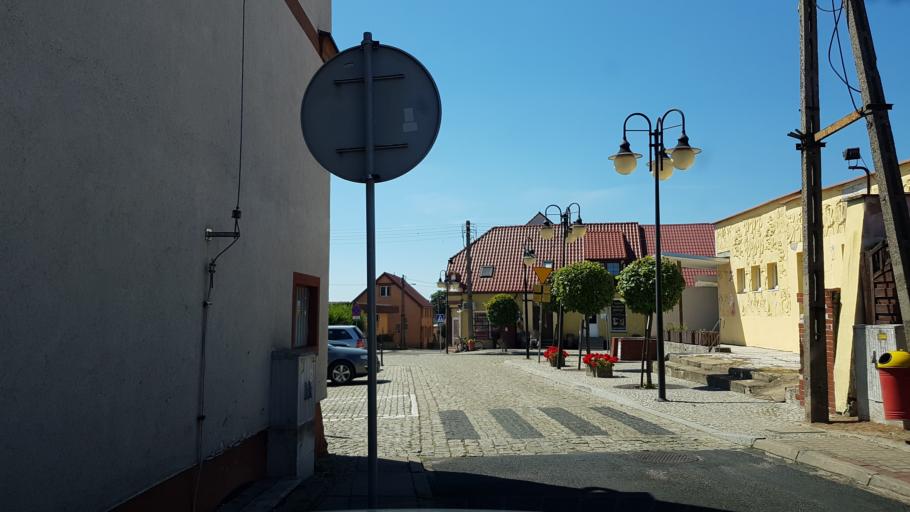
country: PL
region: West Pomeranian Voivodeship
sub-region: Powiat gryfinski
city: Moryn
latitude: 52.8584
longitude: 14.3983
